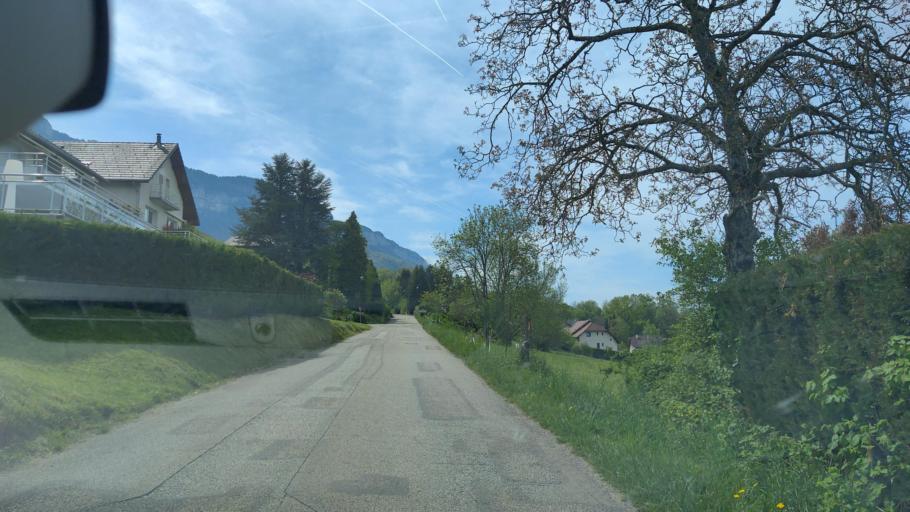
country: FR
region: Rhone-Alpes
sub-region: Departement de la Savoie
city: Mouxy
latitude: 45.6987
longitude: 5.9530
